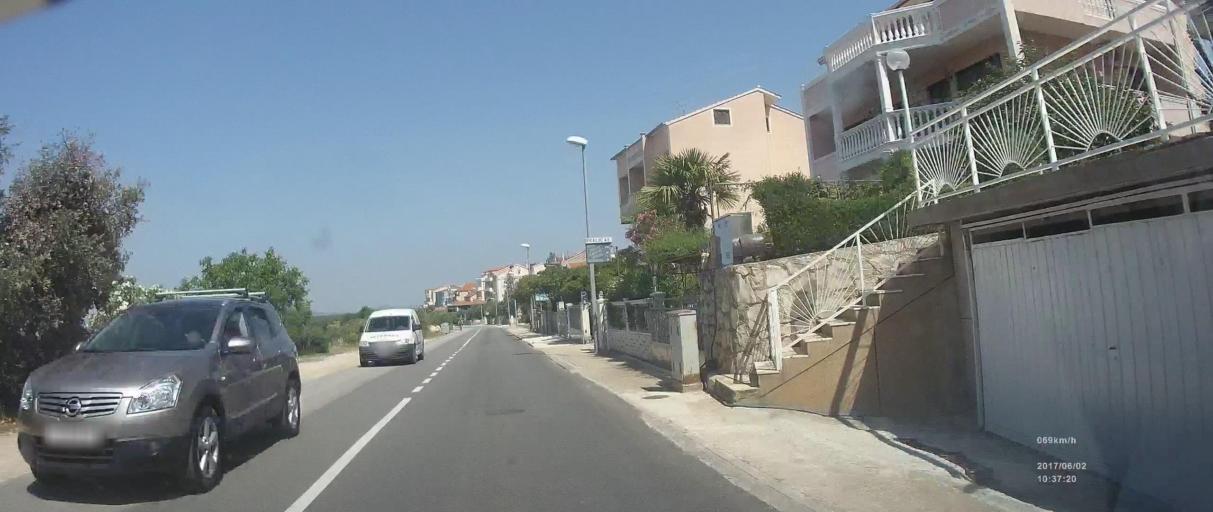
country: HR
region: Sibensko-Kniniska
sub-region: Grad Sibenik
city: Brodarica
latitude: 43.6993
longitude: 15.8988
